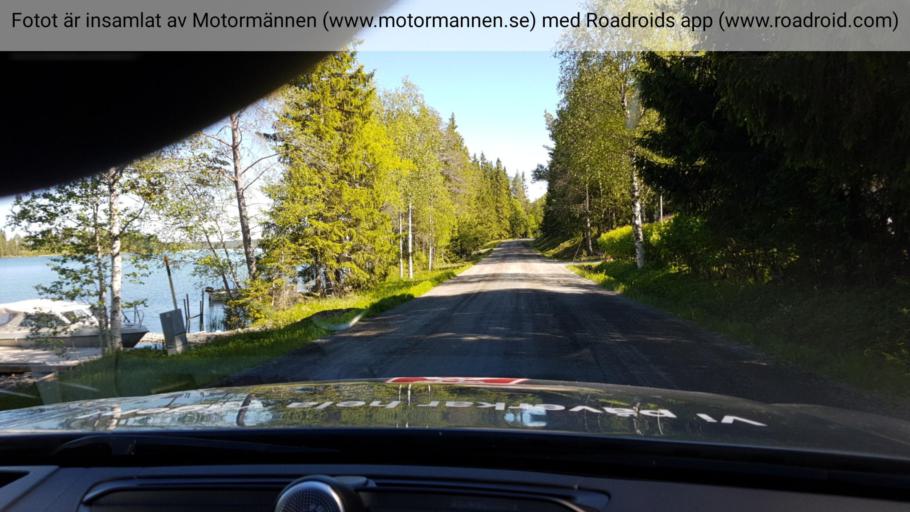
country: SE
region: Jaemtland
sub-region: OEstersunds Kommun
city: Brunflo
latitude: 63.0095
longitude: 14.7842
